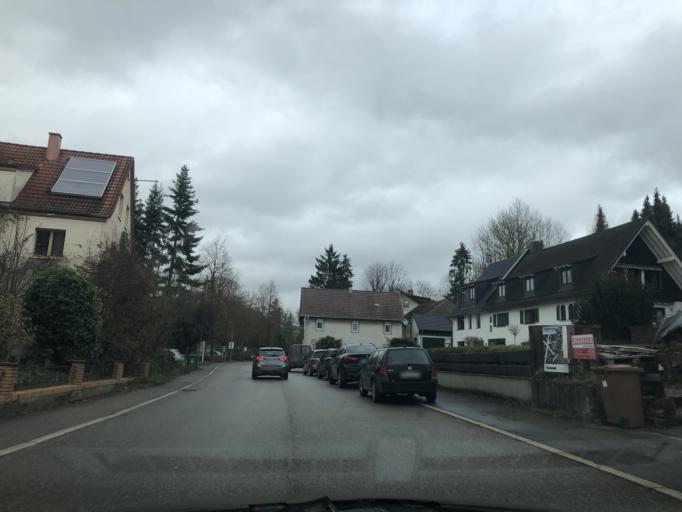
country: DE
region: Baden-Wuerttemberg
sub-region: Karlsruhe Region
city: Dielheim
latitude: 49.3193
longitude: 8.7597
